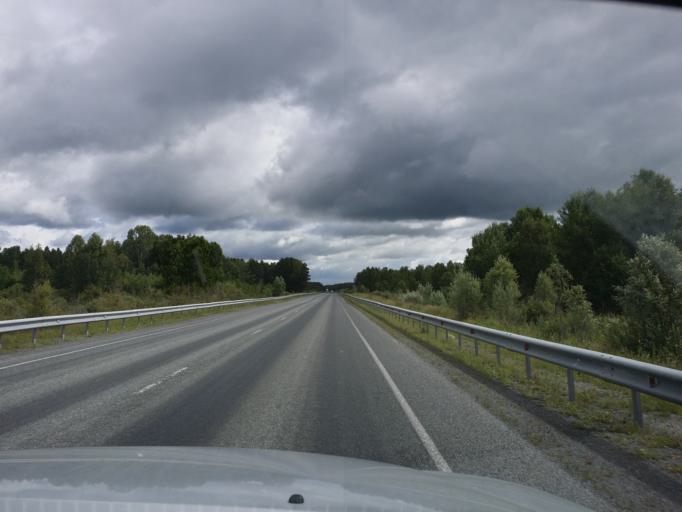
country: RU
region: Tjumen
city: Yarkovo
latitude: 57.5950
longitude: 67.2522
